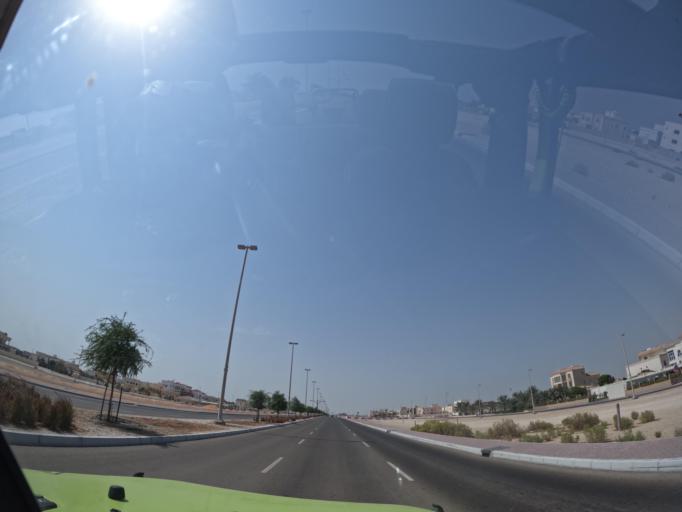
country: AE
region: Abu Dhabi
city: Abu Dhabi
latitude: 24.3527
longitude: 54.6191
